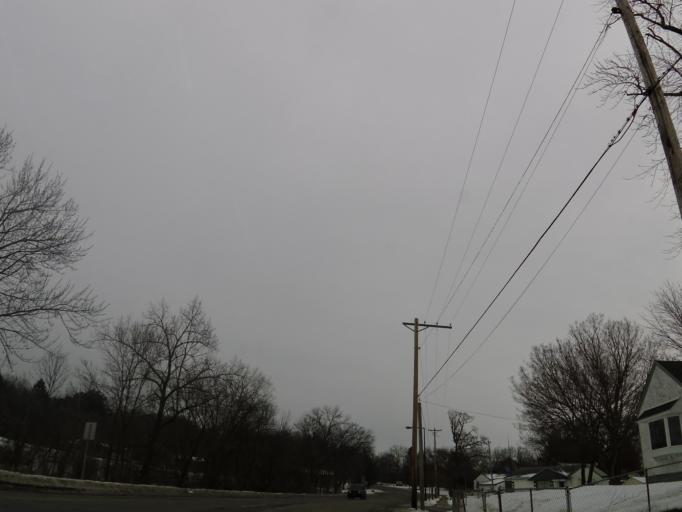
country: US
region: Minnesota
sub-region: Ramsey County
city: Maplewood
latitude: 44.9691
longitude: -93.0069
